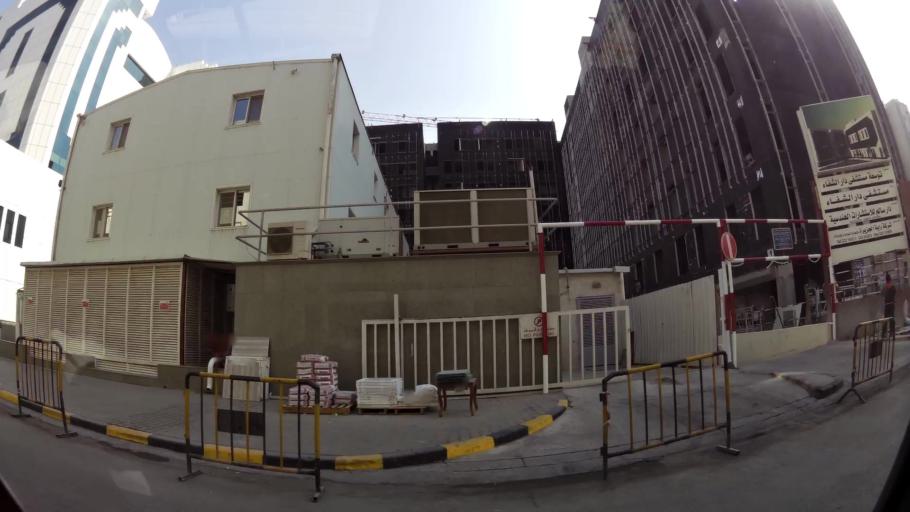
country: KW
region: Muhafazat Hawalli
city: Hawalli
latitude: 29.3349
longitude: 48.0187
